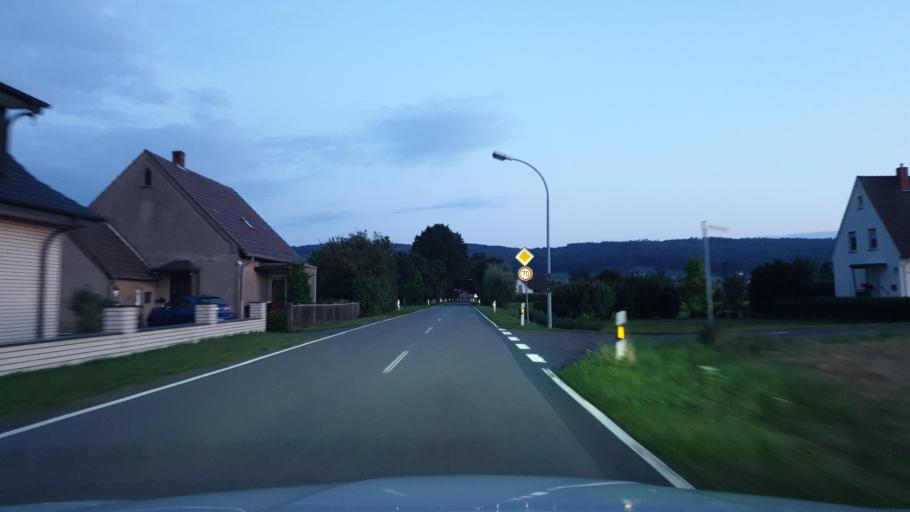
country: DE
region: North Rhine-Westphalia
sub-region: Regierungsbezirk Detmold
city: Huellhorst
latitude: 52.3239
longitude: 8.6680
